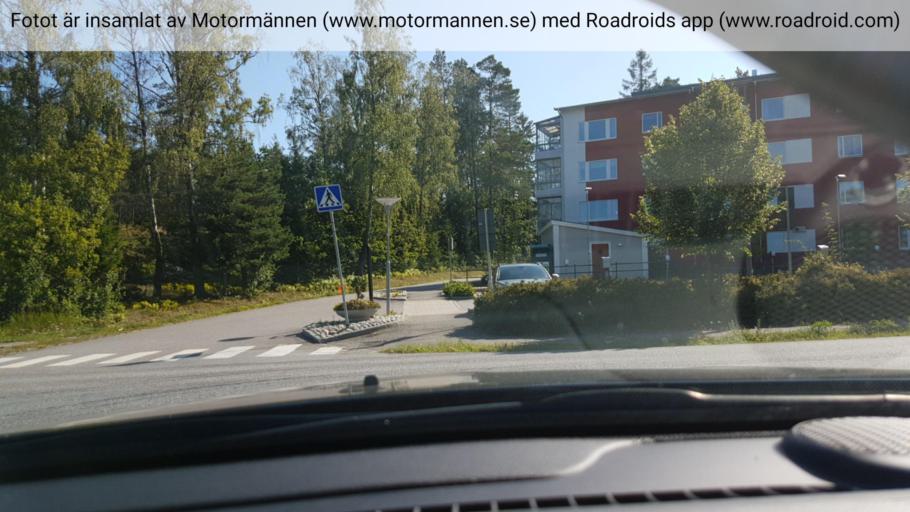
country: SE
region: Stockholm
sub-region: Nynashamns Kommun
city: Osmo
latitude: 58.9823
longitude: 17.8952
